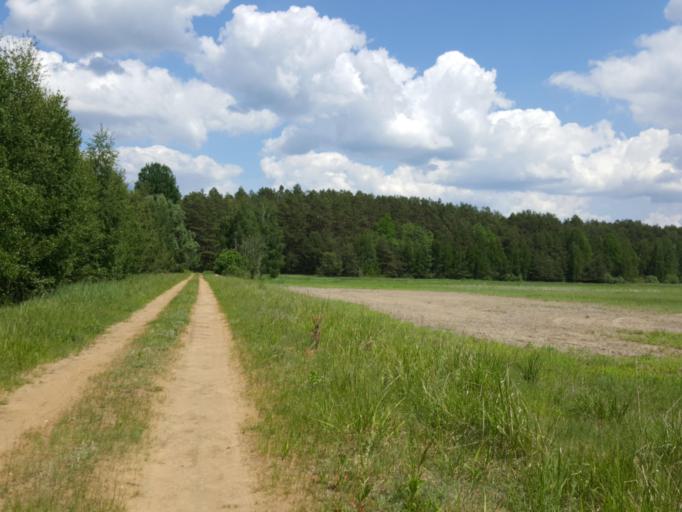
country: BY
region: Brest
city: Kamyanyuki
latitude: 52.5420
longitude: 23.7108
